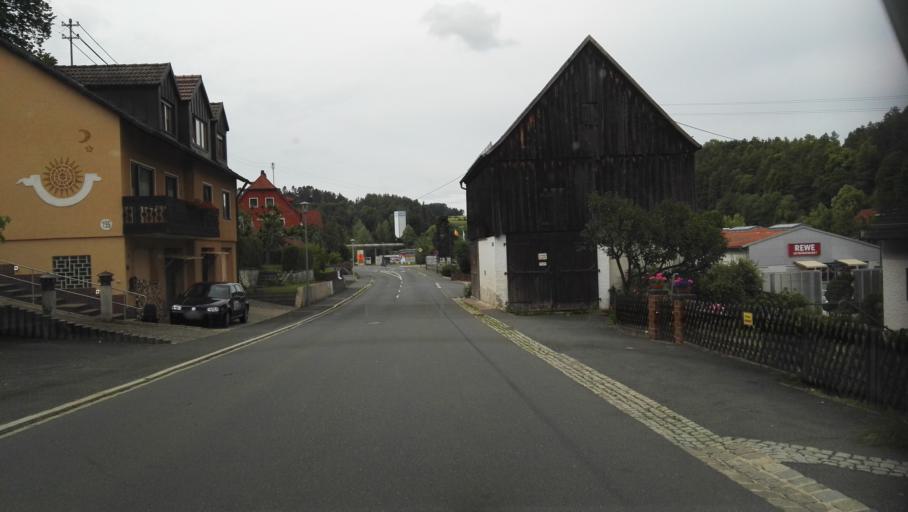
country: DE
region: Bavaria
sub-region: Upper Franconia
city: Waischenfeld
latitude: 49.8474
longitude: 11.3435
